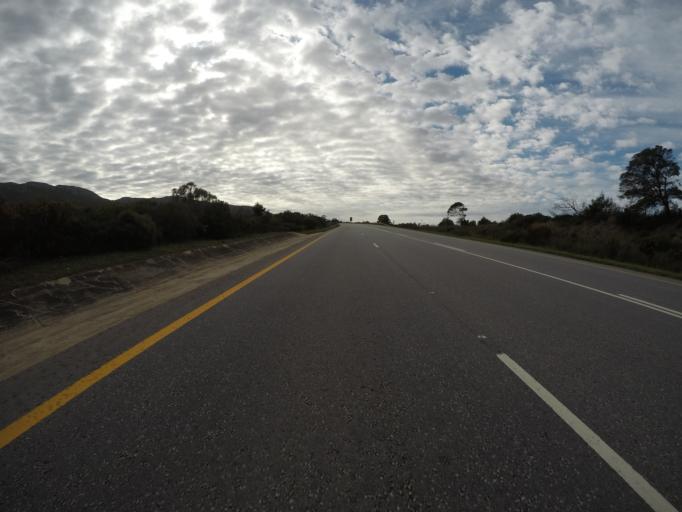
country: ZA
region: Eastern Cape
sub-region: Cacadu District Municipality
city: Kruisfontein
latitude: -34.0056
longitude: 24.6741
